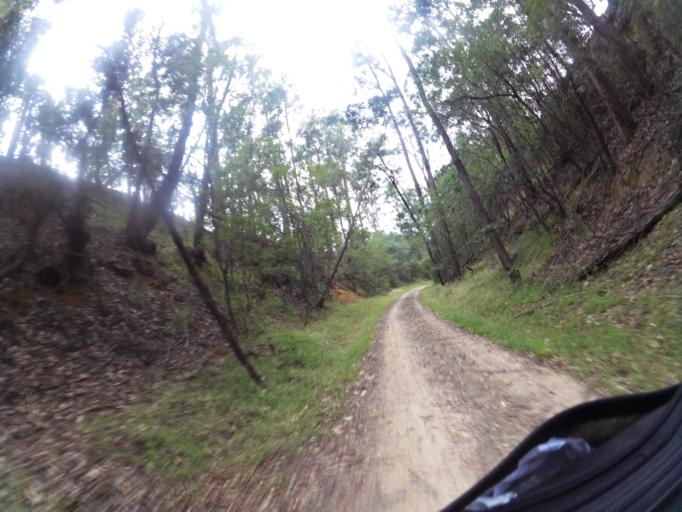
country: AU
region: Victoria
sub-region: East Gippsland
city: Lakes Entrance
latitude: -37.7272
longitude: 148.4256
